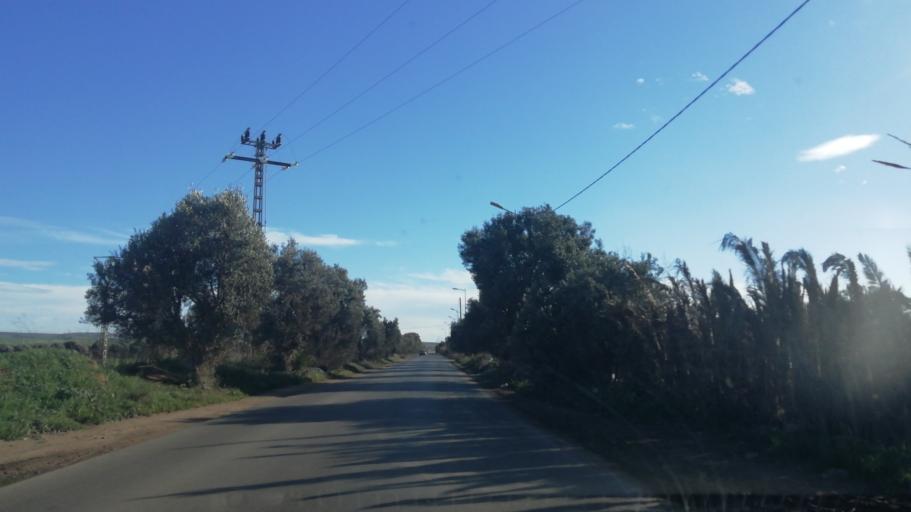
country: DZ
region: Oran
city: Sidi ech Chahmi
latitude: 35.6845
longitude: -0.5038
